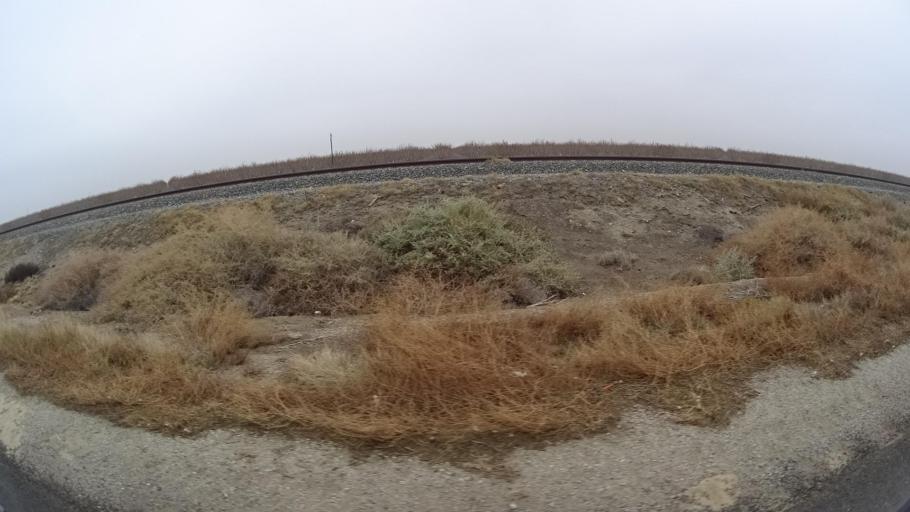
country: US
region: California
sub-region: Kern County
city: Greenfield
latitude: 35.1800
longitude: -119.1501
